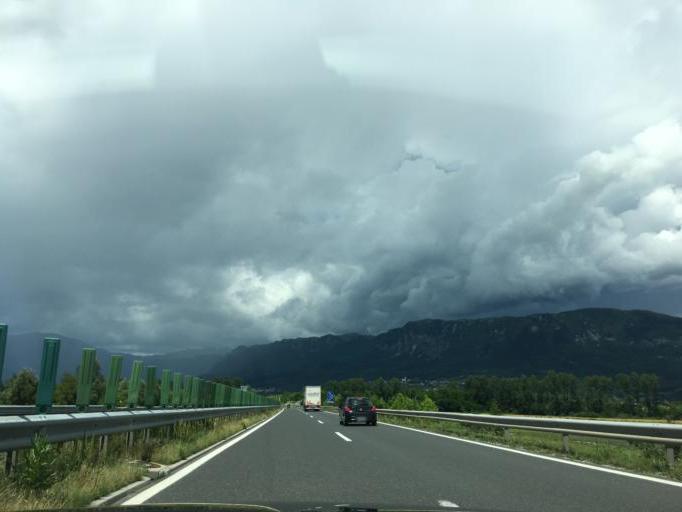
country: SI
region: Vipava
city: Vipava
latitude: 45.8399
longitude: 13.9528
